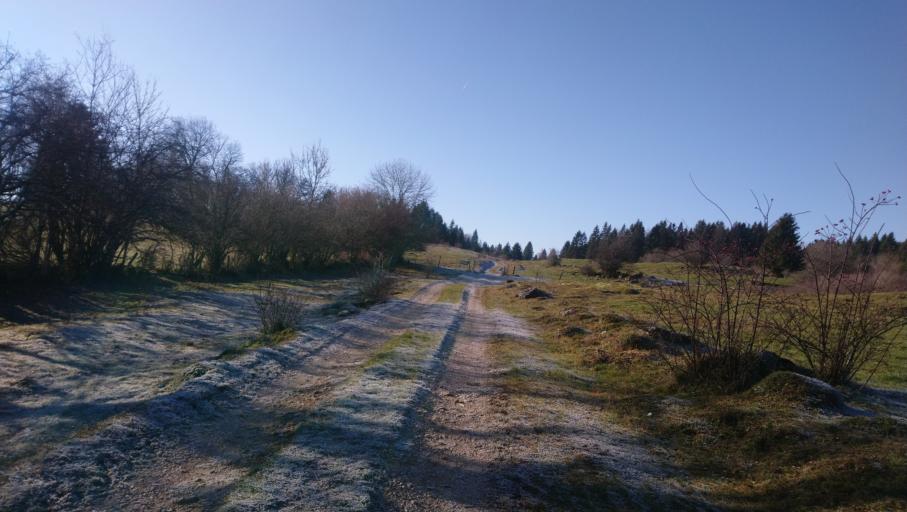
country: FR
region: Franche-Comte
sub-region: Departement du Doubs
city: Pontarlier
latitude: 46.8400
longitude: 6.2750
